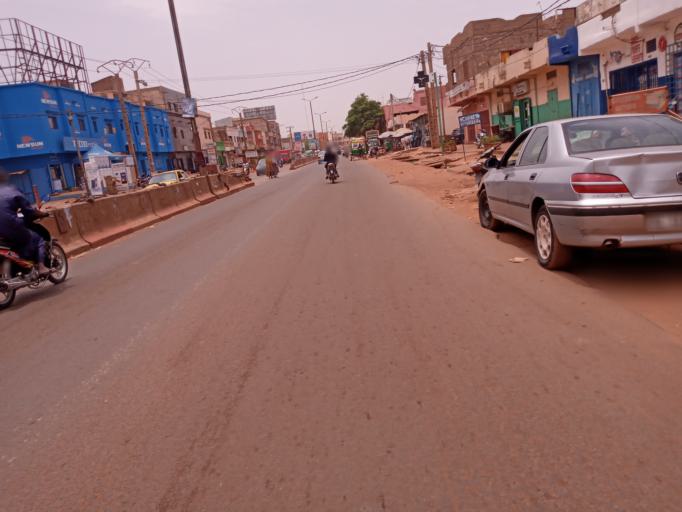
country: ML
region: Bamako
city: Bamako
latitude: 12.6004
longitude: -8.0126
